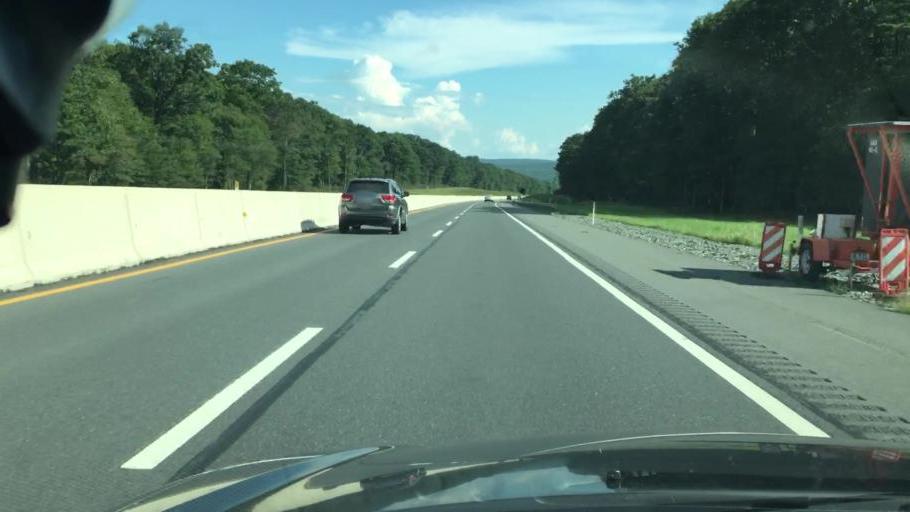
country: US
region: Pennsylvania
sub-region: Carbon County
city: Towamensing Trails
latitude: 41.0273
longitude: -75.6503
